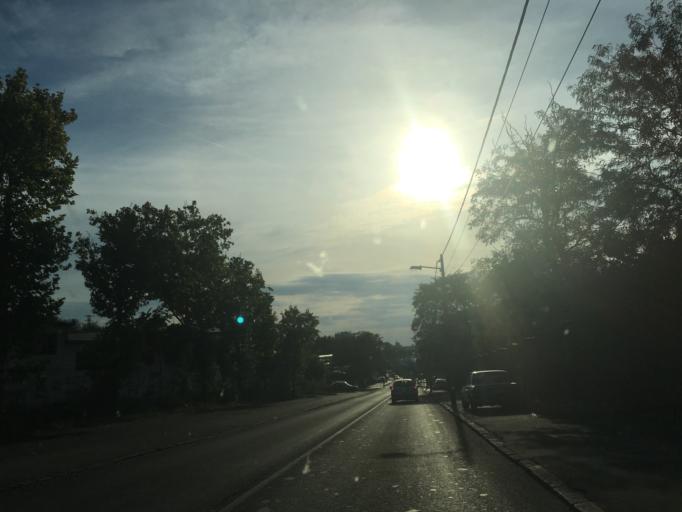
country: RS
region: Central Serbia
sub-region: Belgrade
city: Palilula
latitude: 44.8136
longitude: 20.4994
